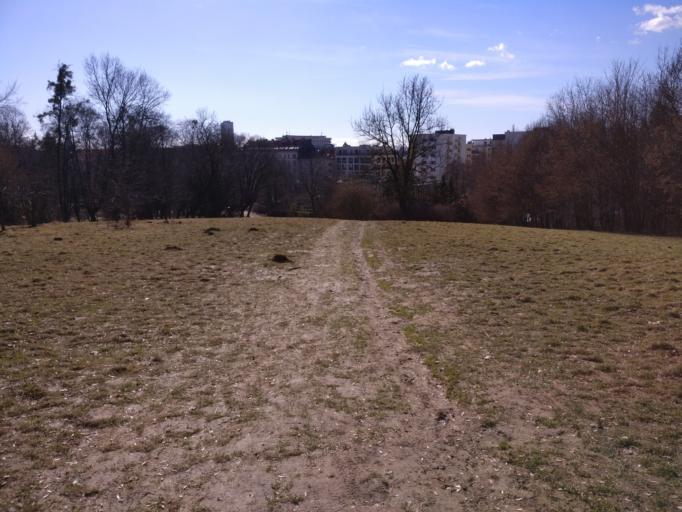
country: AT
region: Styria
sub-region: Graz Stadt
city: Graz
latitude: 47.0836
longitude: 15.4481
